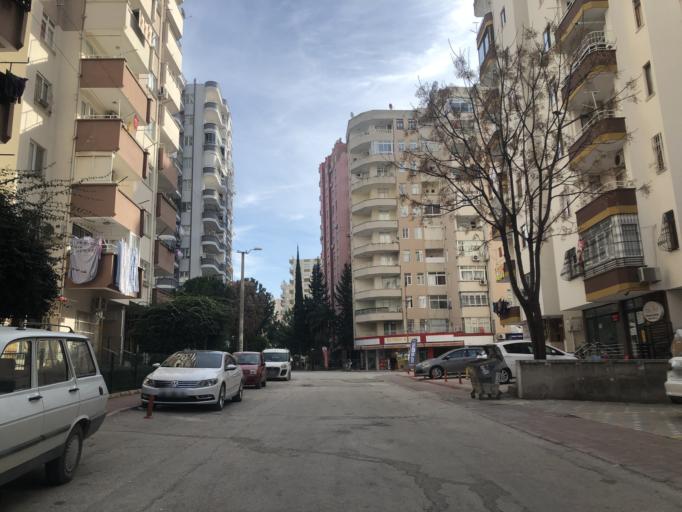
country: TR
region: Adana
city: Adana
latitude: 37.0517
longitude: 35.2896
